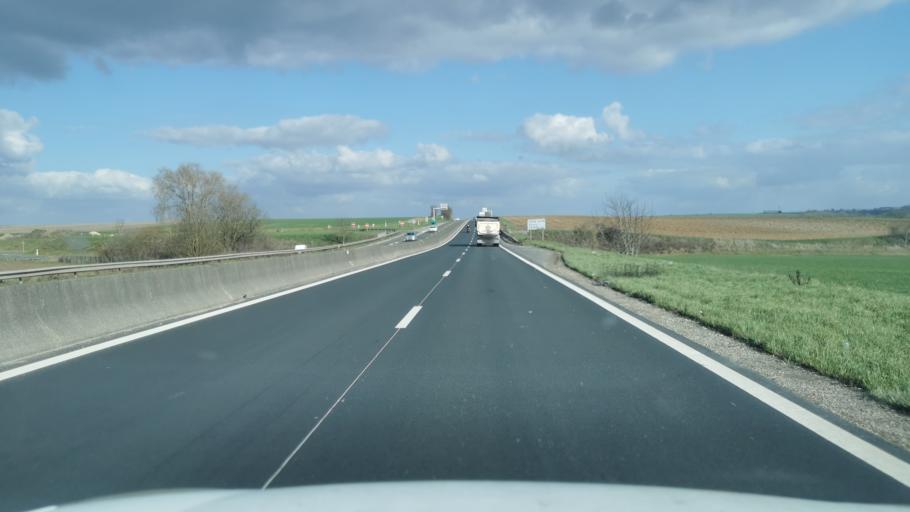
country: FR
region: Ile-de-France
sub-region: Departement de Seine-et-Marne
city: Charny
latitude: 48.9517
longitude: 2.7689
